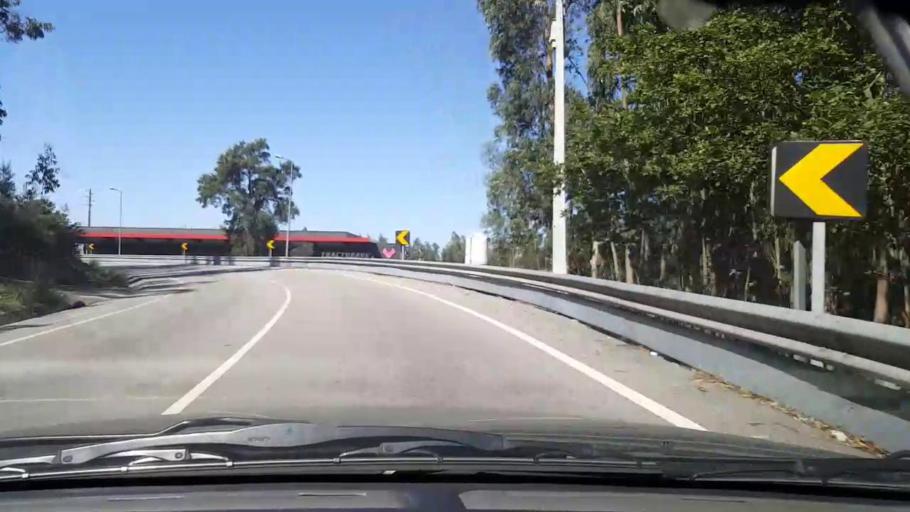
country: PT
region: Porto
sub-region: Vila do Conde
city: Arvore
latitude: 41.3426
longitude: -8.6562
